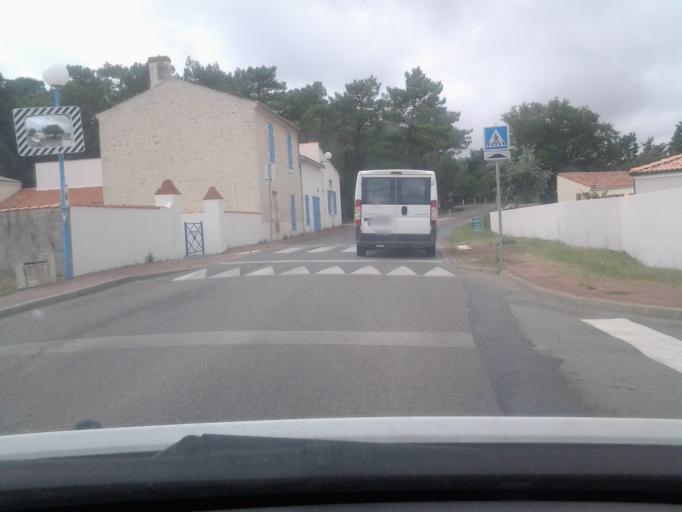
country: FR
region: Pays de la Loire
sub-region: Departement de la Vendee
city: Longeville-sur-Mer
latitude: 46.3893
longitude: -1.4712
